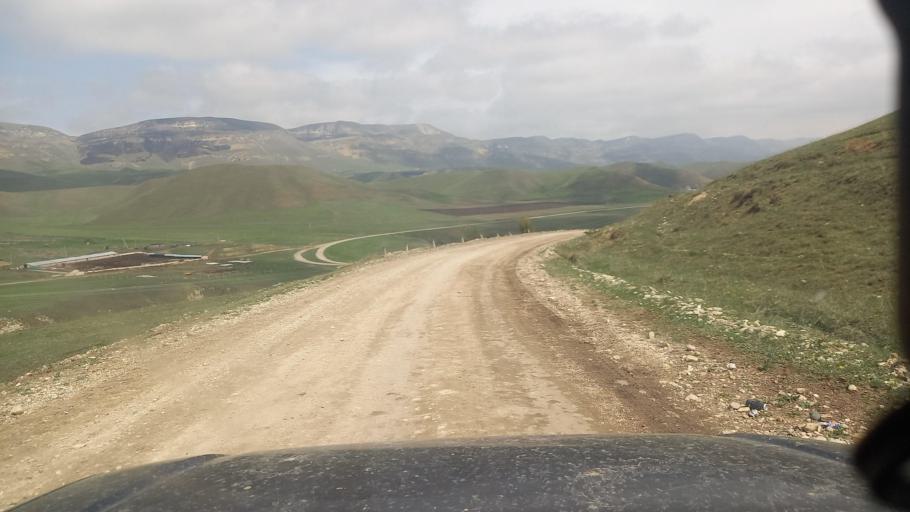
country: RU
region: Kabardino-Balkariya
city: Kamennomostskoye
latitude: 43.7979
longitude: 42.9024
